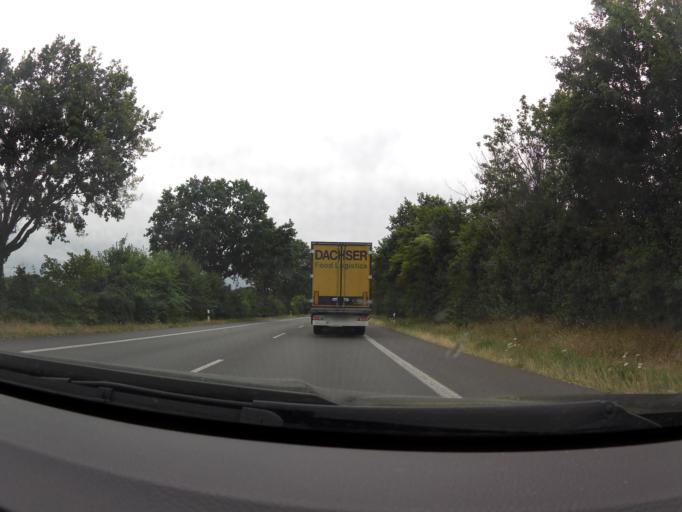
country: DE
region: North Rhine-Westphalia
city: Straelen
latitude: 51.4396
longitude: 6.2808
